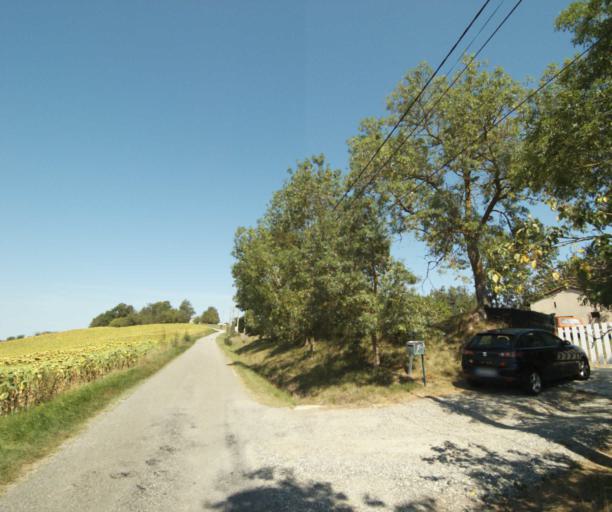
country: FR
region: Midi-Pyrenees
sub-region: Departement de l'Ariege
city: Lezat-sur-Leze
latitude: 43.2585
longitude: 1.3918
